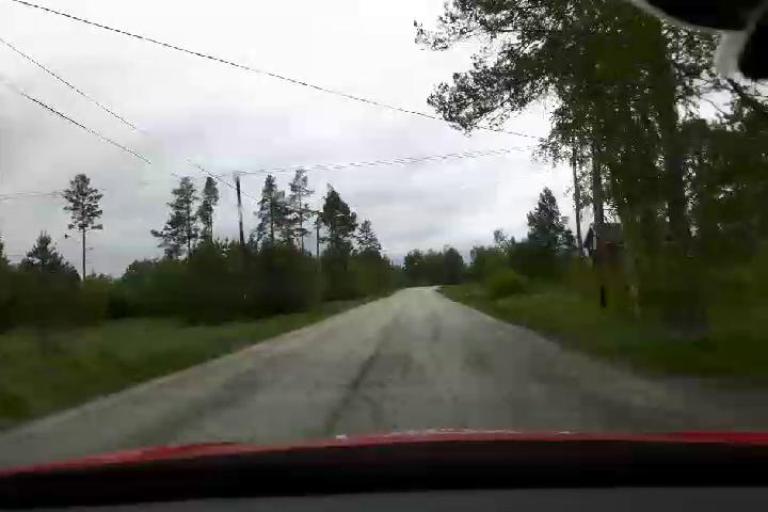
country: SE
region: Jaemtland
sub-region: Bergs Kommun
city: Hoverberg
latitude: 62.7393
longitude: 14.4230
